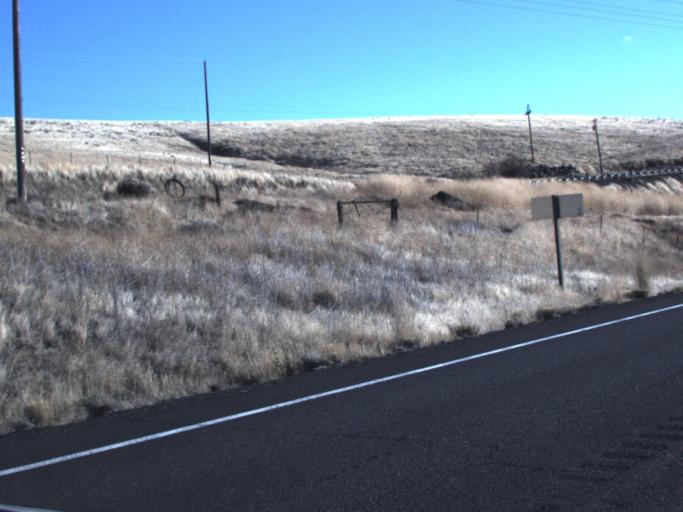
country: US
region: Washington
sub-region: Garfield County
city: Pomeroy
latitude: 46.4668
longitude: -117.4794
